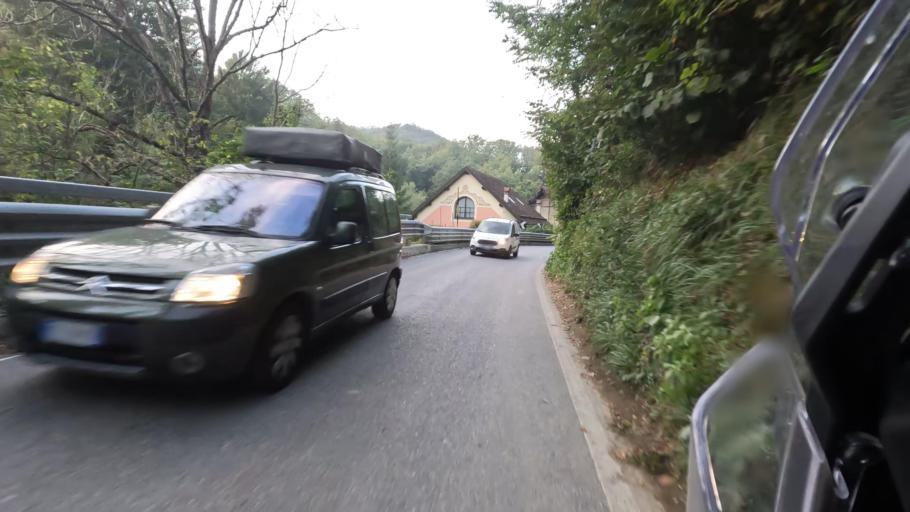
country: IT
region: Liguria
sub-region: Provincia di Savona
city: Sassello
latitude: 44.4645
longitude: 8.4826
